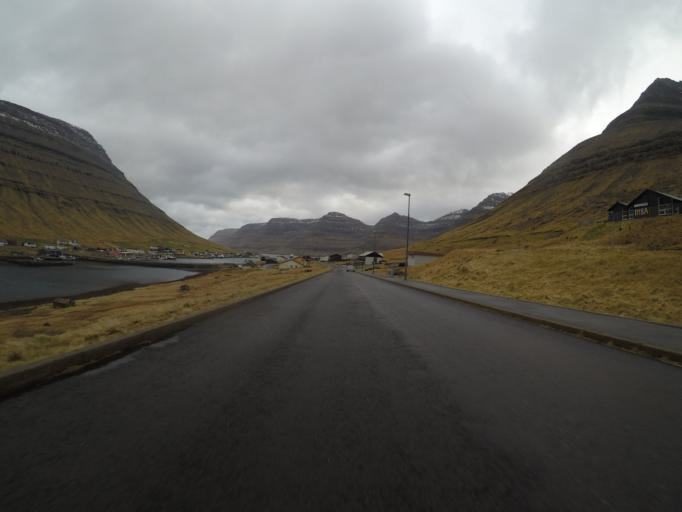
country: FO
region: Nordoyar
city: Klaksvik
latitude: 62.3009
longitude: -6.5316
